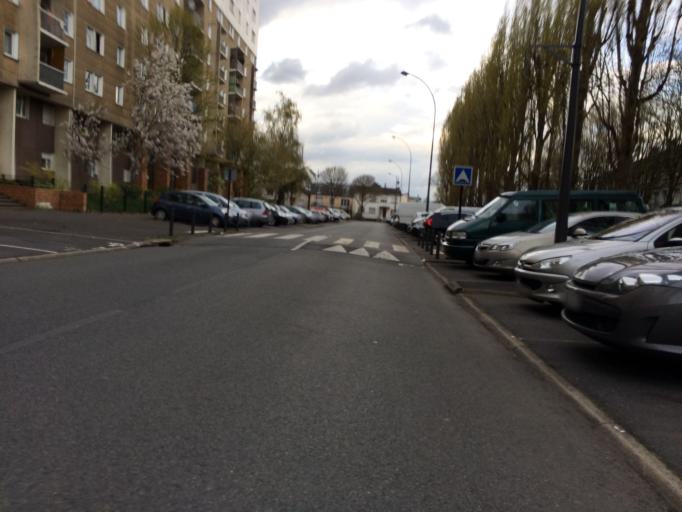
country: FR
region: Ile-de-France
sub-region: Departement des Hauts-de-Seine
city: Antony
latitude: 48.7369
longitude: 2.2978
